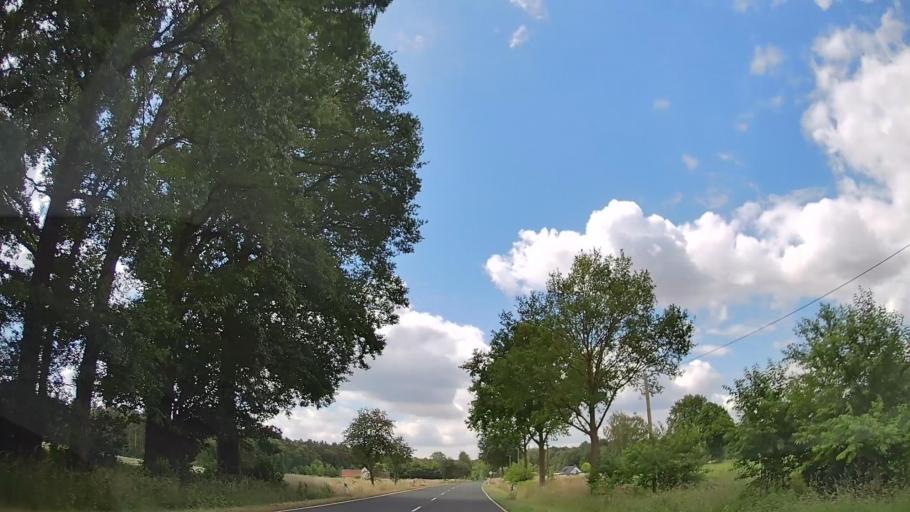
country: DE
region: North Rhine-Westphalia
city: Rahden
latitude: 52.4083
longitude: 8.5209
